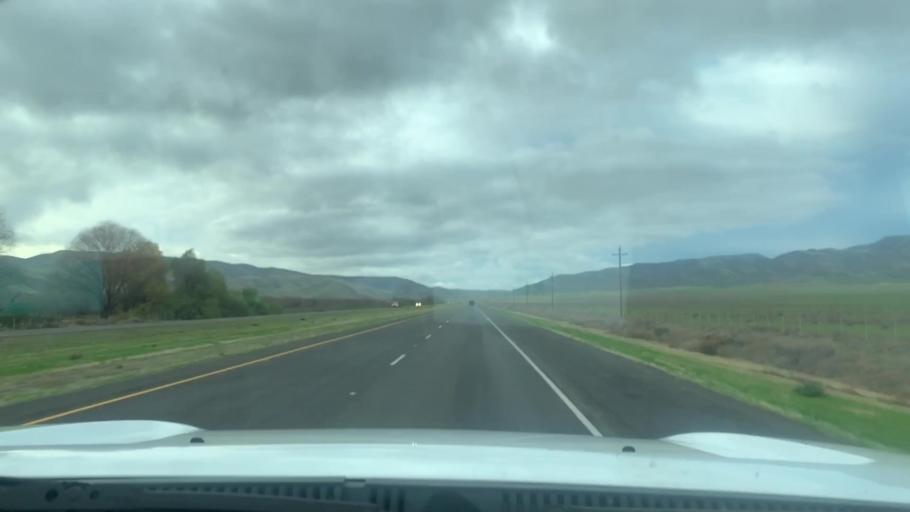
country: US
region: California
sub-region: San Luis Obispo County
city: Shandon
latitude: 35.6787
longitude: -120.0977
